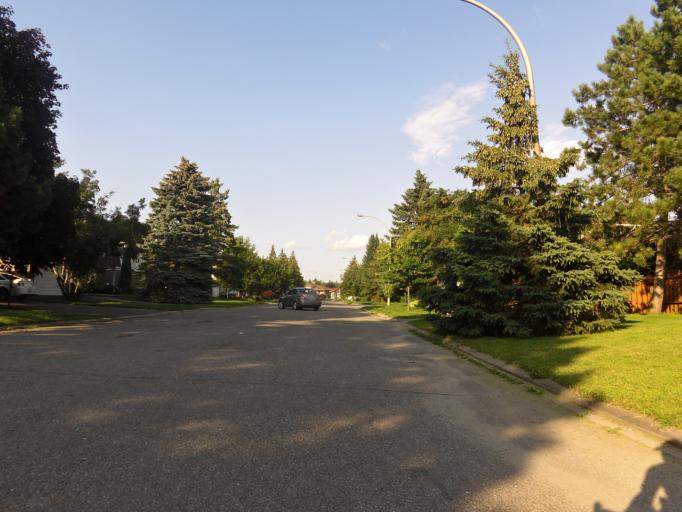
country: CA
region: Ontario
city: Bells Corners
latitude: 45.3311
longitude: -75.7927
